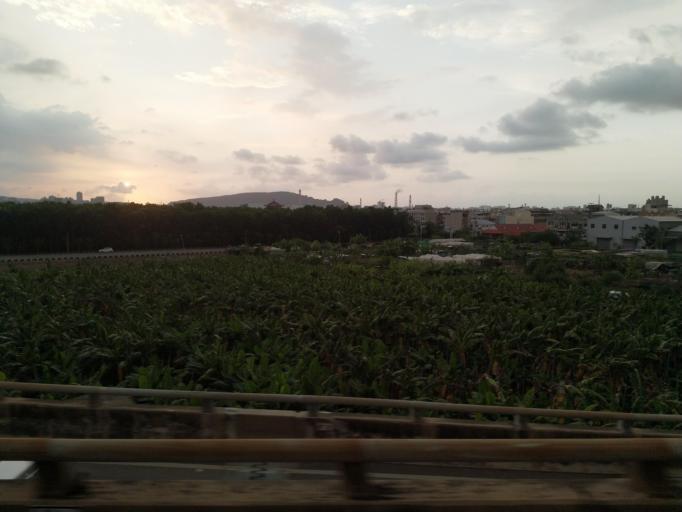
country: TW
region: Taiwan
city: Fengshan
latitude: 22.6977
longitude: 120.3586
